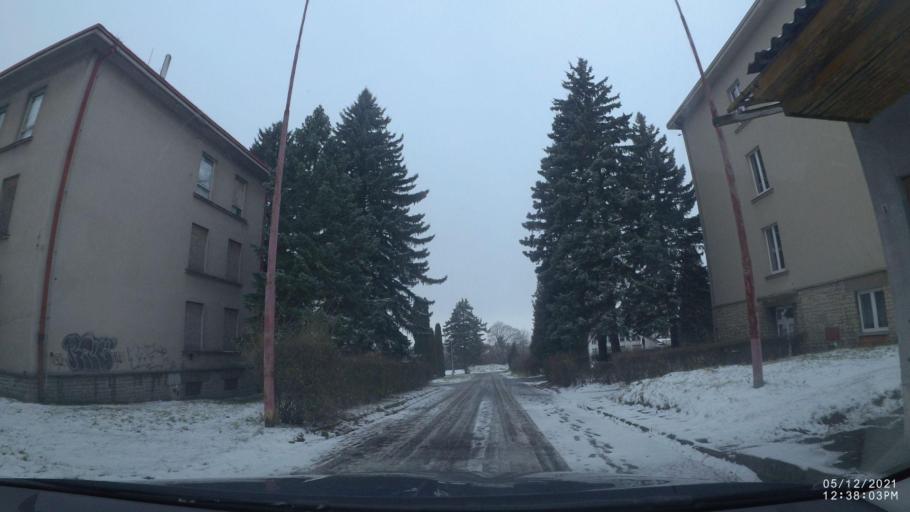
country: CZ
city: Nove Mesto nad Metuji
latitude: 50.3551
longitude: 16.1525
